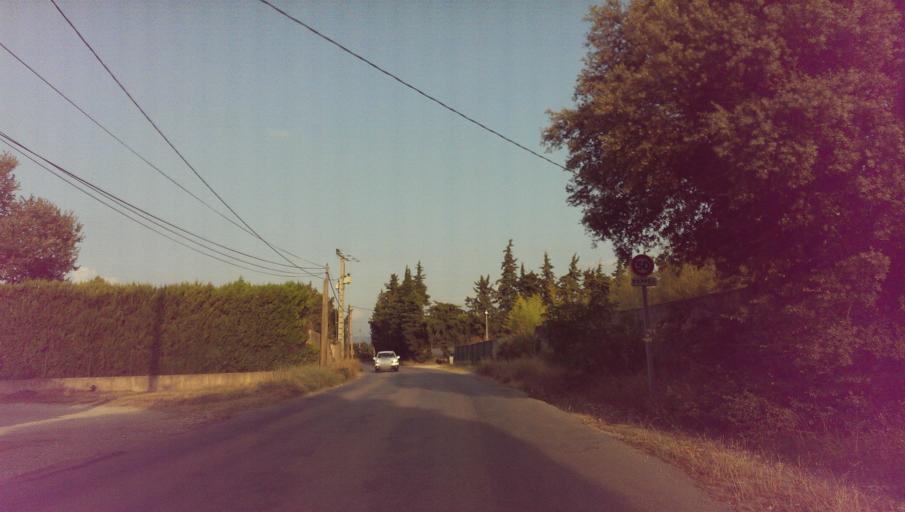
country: FR
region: Provence-Alpes-Cote d'Azur
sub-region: Departement du Vaucluse
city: Carpentras
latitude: 44.0304
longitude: 5.0655
